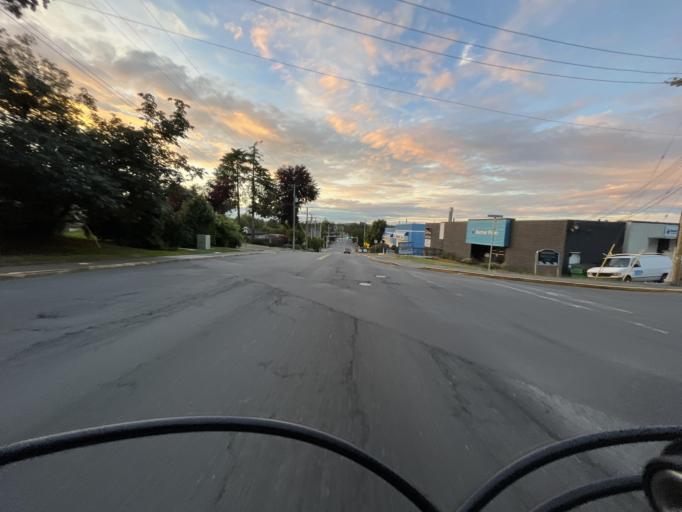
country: CA
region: British Columbia
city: Victoria
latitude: 48.4357
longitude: -123.4030
